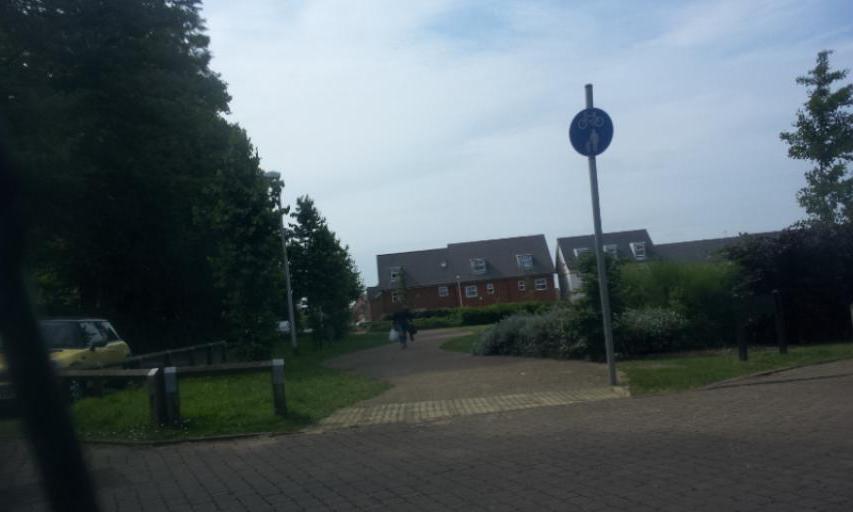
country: GB
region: England
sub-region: Kent
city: Gillingham
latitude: 51.3873
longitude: 0.5769
